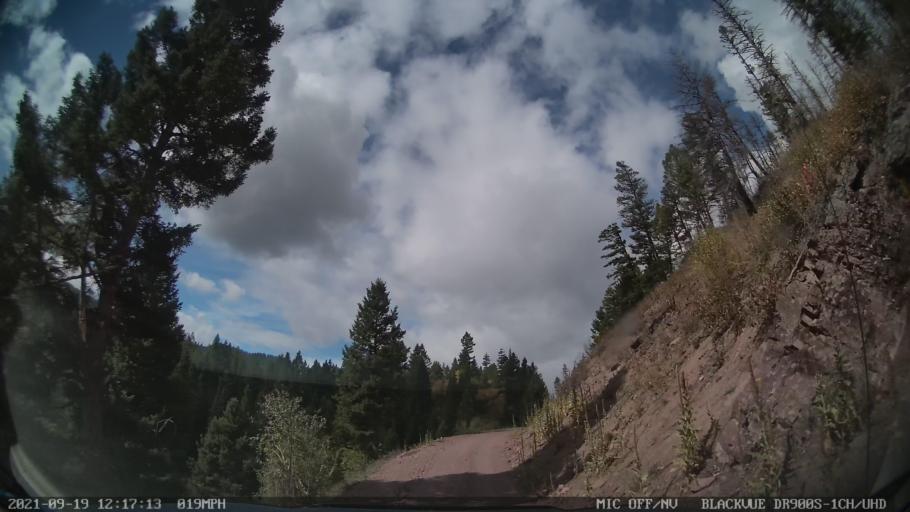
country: US
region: Montana
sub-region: Missoula County
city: Seeley Lake
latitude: 47.1716
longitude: -113.3567
